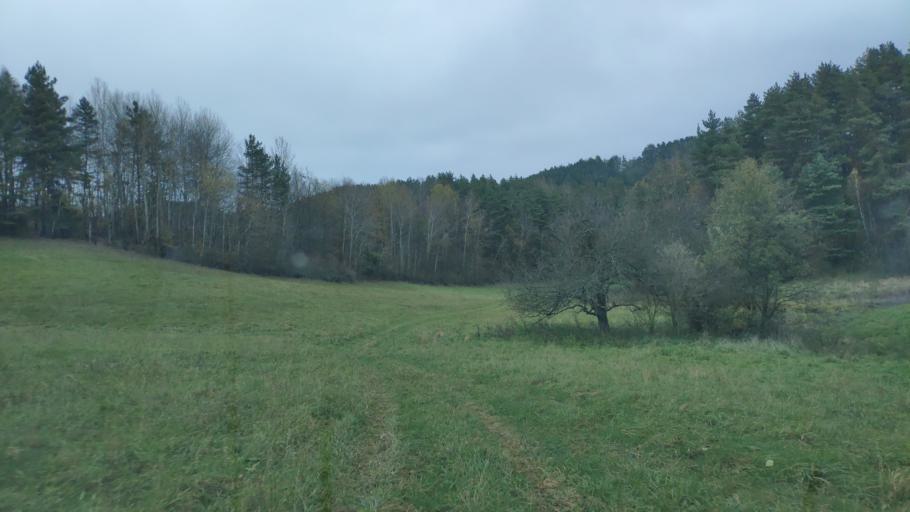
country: SK
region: Presovsky
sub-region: Okres Presov
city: Presov
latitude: 48.9292
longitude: 21.1011
